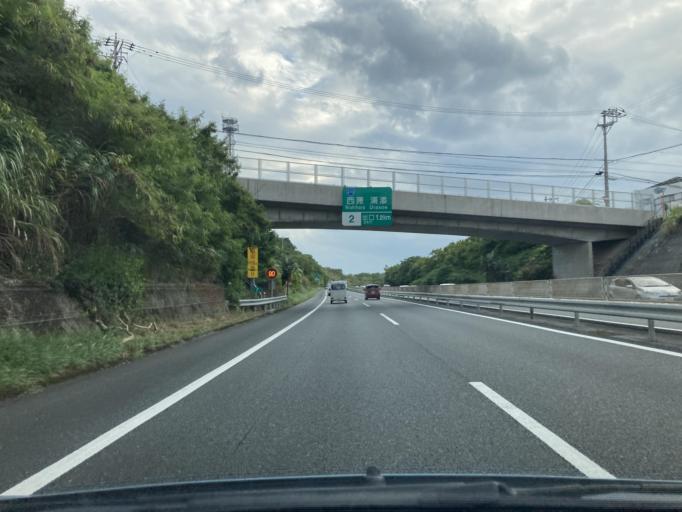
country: JP
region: Okinawa
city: Ginowan
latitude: 26.2541
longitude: 127.7623
